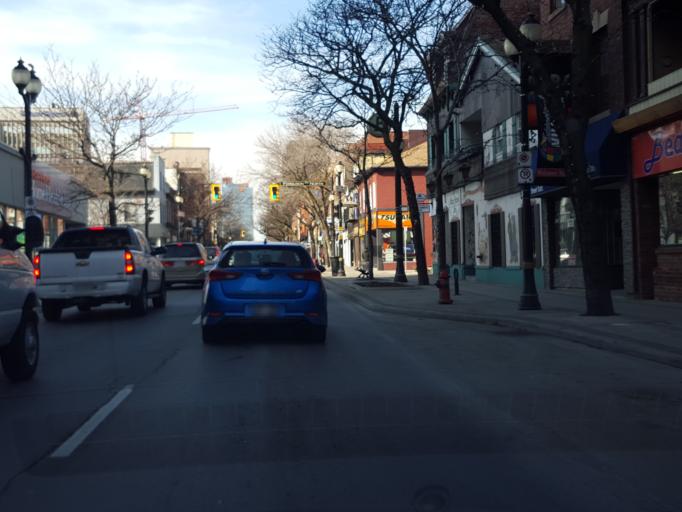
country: CA
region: Ontario
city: Hamilton
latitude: 43.2541
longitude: -79.8612
